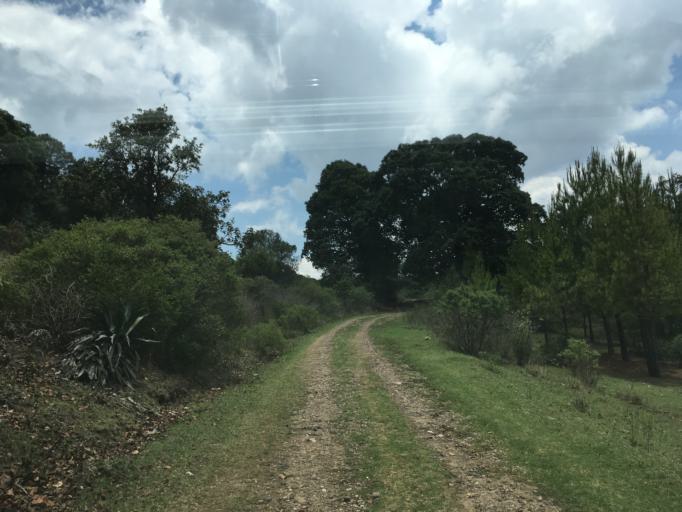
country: MX
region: Oaxaca
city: San Andres Sinaxtla
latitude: 17.6082
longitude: -97.2618
